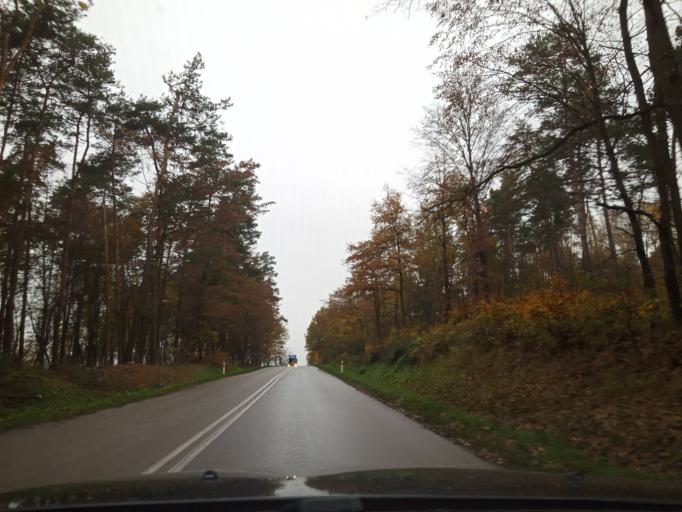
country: PL
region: Swietokrzyskie
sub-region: Powiat pinczowski
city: Dzialoszyce
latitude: 50.4561
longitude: 20.3647
